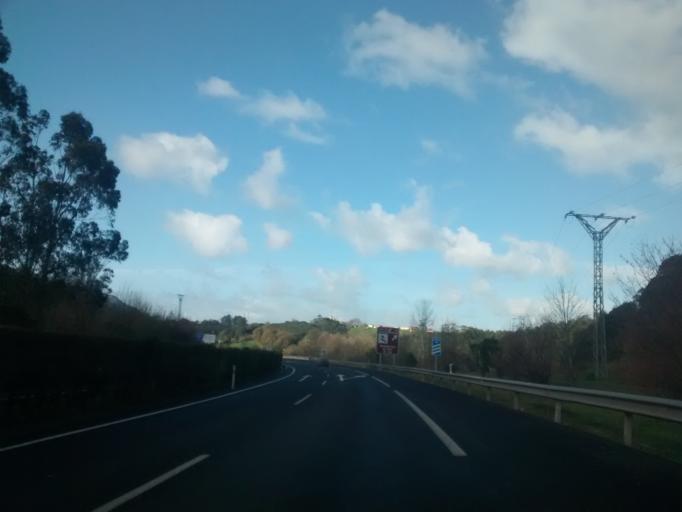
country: ES
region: Cantabria
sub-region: Provincia de Cantabria
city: Entrambasaguas
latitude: 43.3918
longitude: -3.6975
